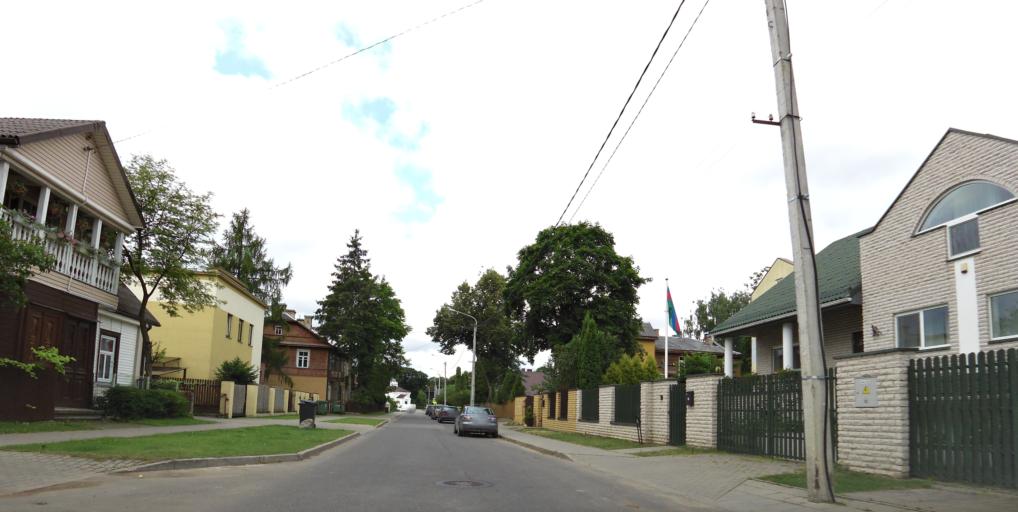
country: LT
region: Vilnius County
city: Seskine
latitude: 54.6930
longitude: 25.2479
